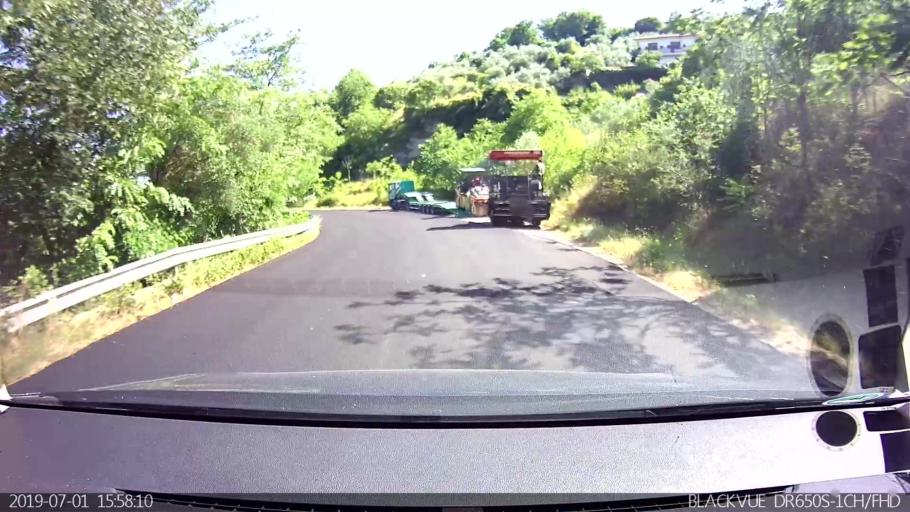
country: IT
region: Latium
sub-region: Provincia di Frosinone
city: Sant'Angelo in Villa-Giglio
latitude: 41.6700
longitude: 13.4216
